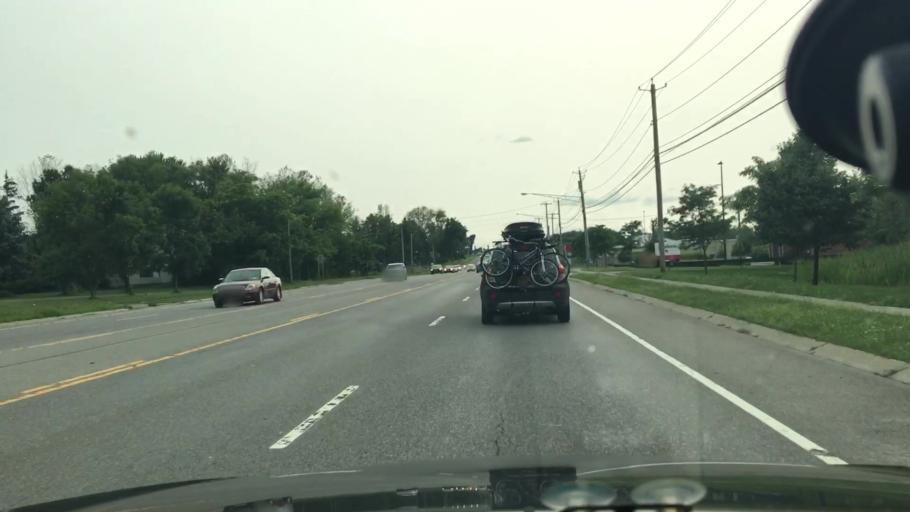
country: US
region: New York
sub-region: Erie County
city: Wanakah
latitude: 42.7429
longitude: -78.8673
